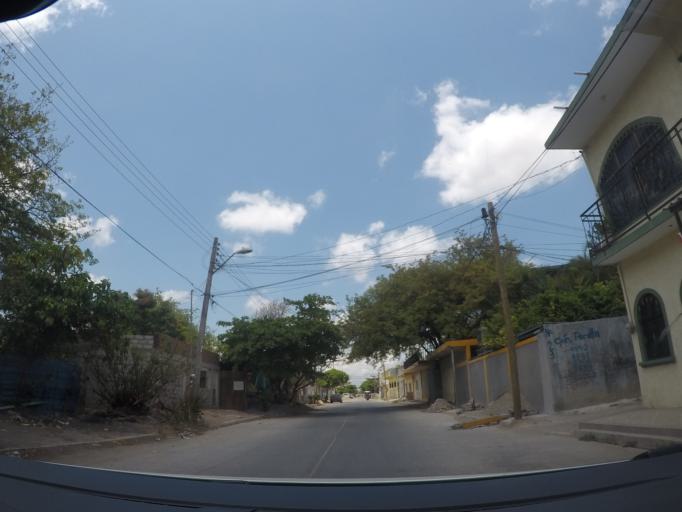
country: MX
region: Oaxaca
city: Juchitan de Zaragoza
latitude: 16.4409
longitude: -95.0171
